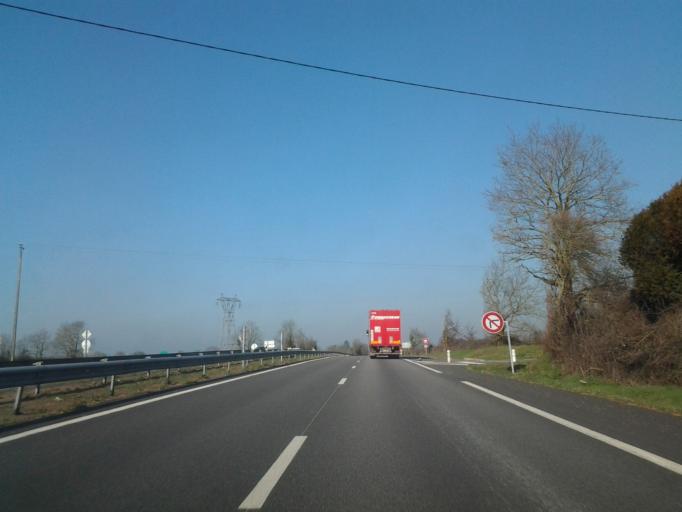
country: FR
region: Pays de la Loire
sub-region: Departement de la Vendee
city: Mouilleron-le-Captif
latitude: 46.6894
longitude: -1.4634
